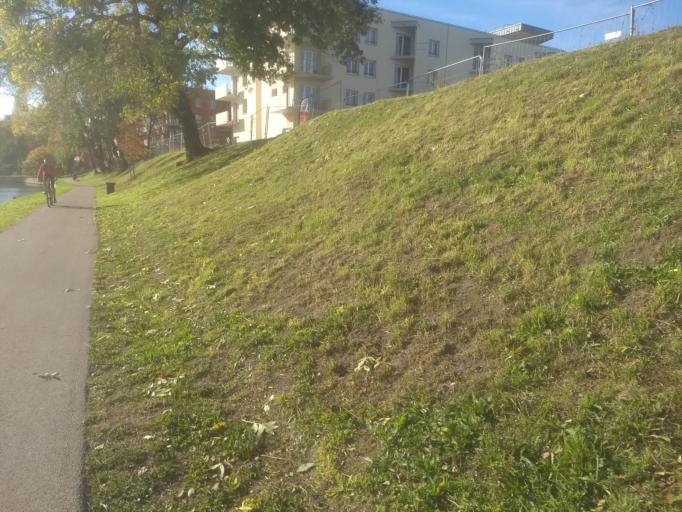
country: FR
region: Nord-Pas-de-Calais
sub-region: Departement du Pas-de-Calais
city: Arras
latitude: 50.2966
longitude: 2.7741
